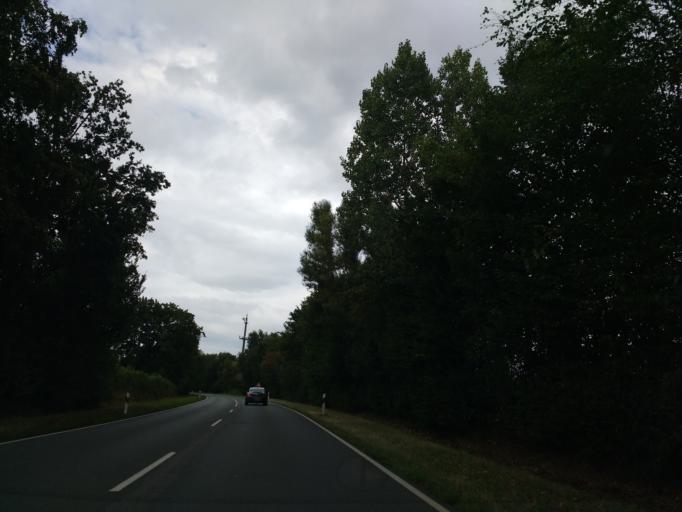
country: DE
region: Lower Saxony
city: Bad Rothenfelde
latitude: 52.1052
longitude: 8.1759
